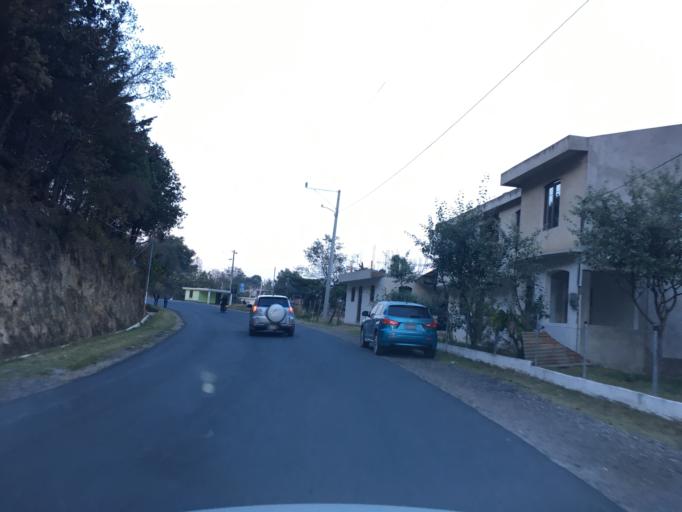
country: GT
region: Chimaltenango
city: Tecpan Guatemala
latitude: 14.7458
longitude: -91.0011
